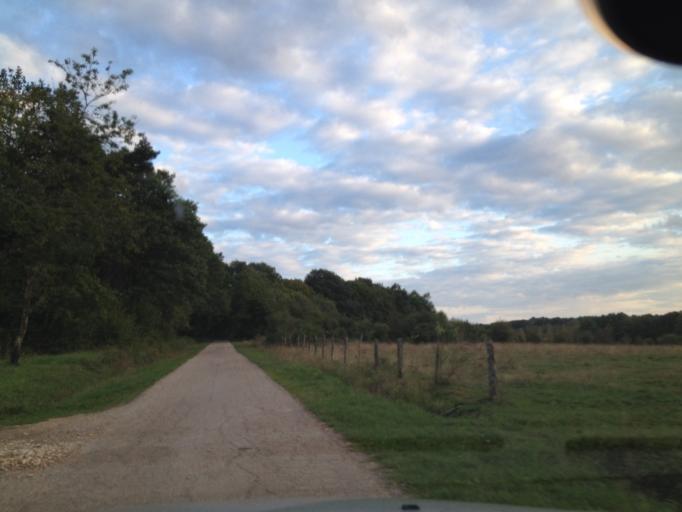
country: FR
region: Lorraine
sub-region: Departement des Vosges
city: Bains-les-Bains
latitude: 47.9609
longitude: 6.1702
